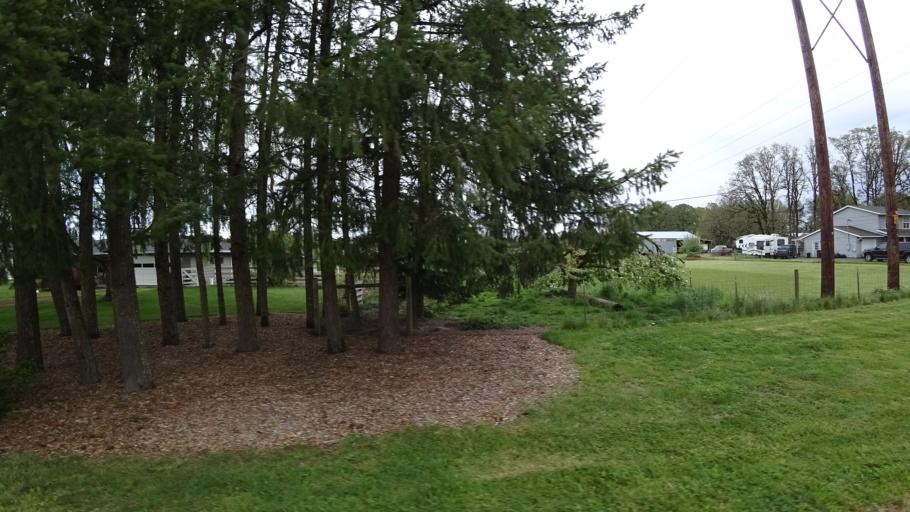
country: US
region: Oregon
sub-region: Washington County
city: Hillsboro
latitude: 45.5575
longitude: -122.9584
